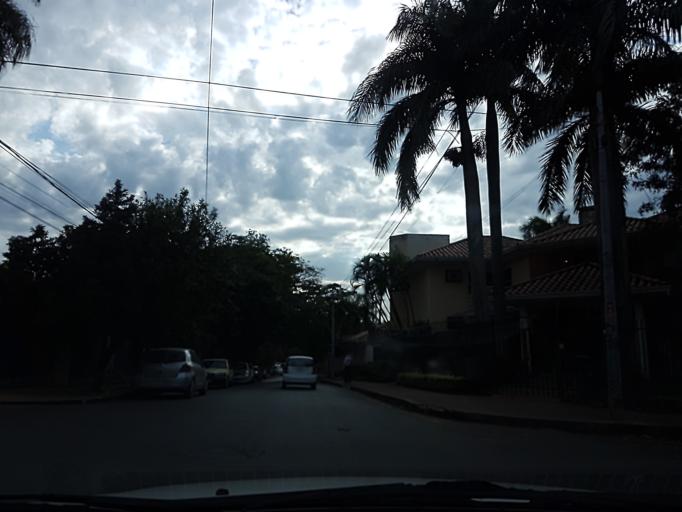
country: PY
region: Asuncion
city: Asuncion
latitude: -25.2989
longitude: -57.5874
